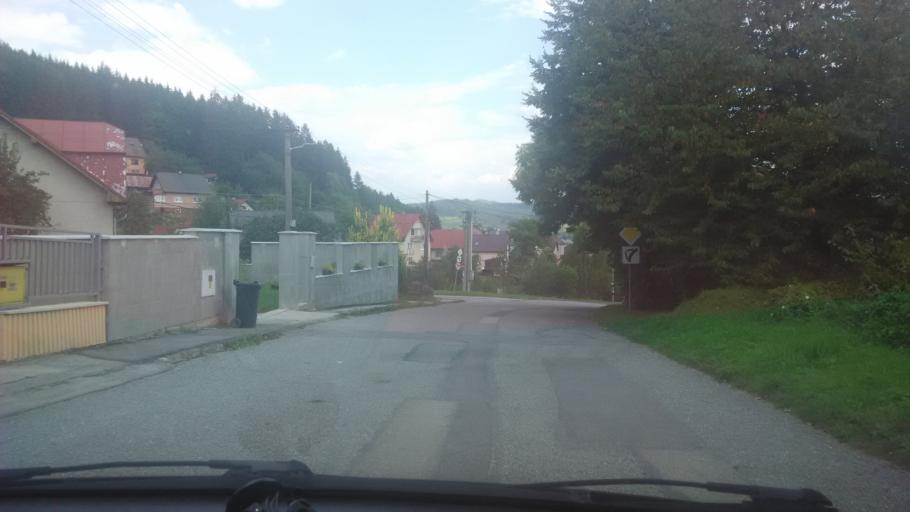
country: SK
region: Zilinsky
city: Kysucke Nove Mesto
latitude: 49.3070
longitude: 18.7673
